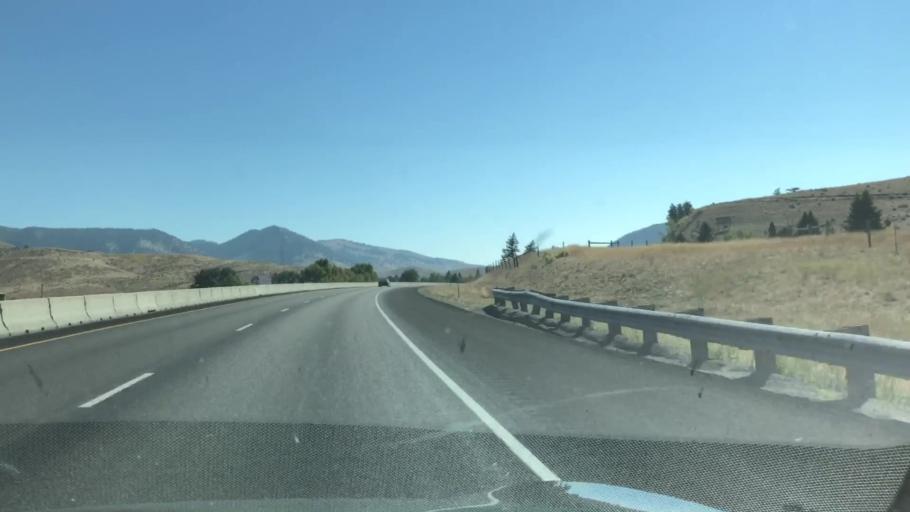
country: US
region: Montana
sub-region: Granite County
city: Philipsburg
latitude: 46.7126
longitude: -113.2714
